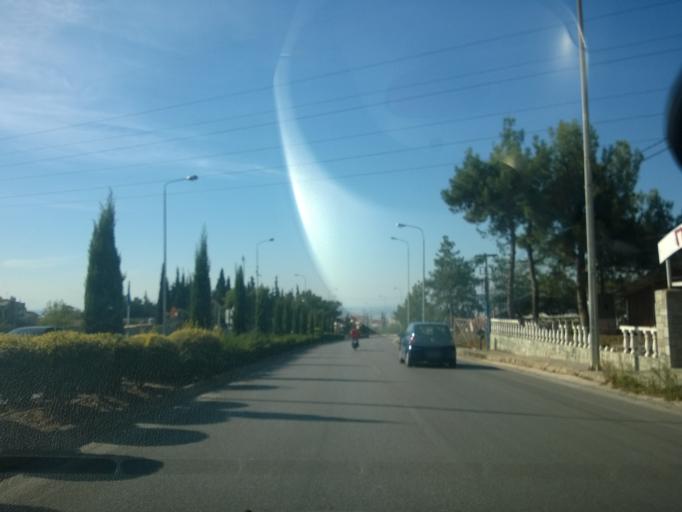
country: GR
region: Central Macedonia
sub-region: Nomos Thessalonikis
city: Pylaia
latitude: 40.5986
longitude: 22.9983
